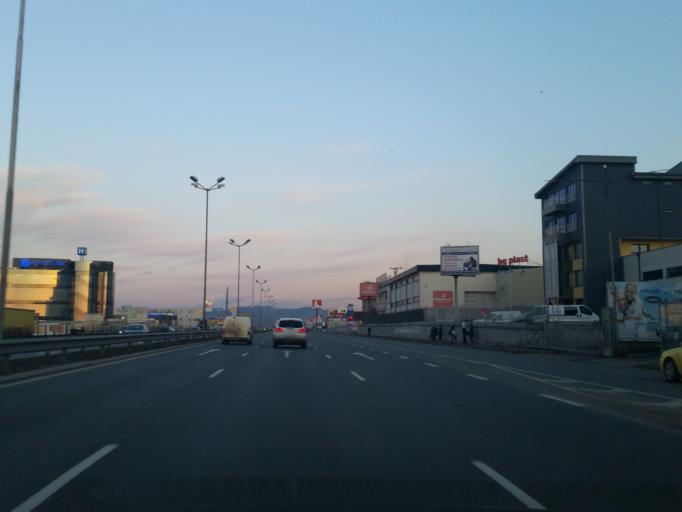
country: BG
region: Sofia-Capital
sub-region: Stolichna Obshtina
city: Sofia
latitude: 42.6404
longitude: 23.3154
